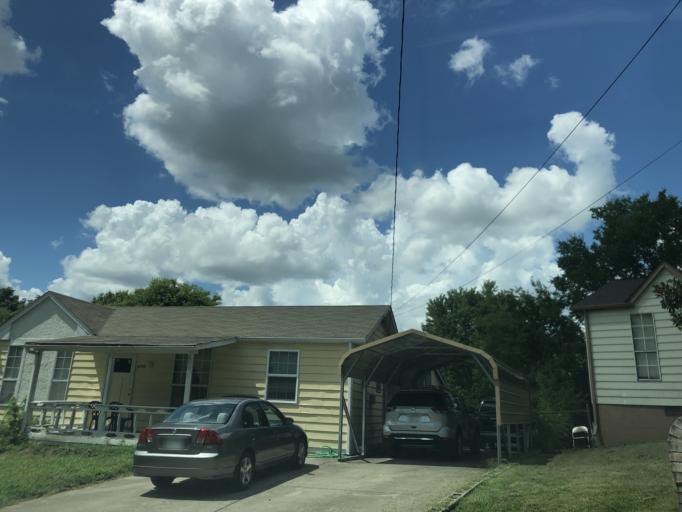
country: US
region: Tennessee
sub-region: Davidson County
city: Oak Hill
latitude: 36.0732
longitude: -86.7178
